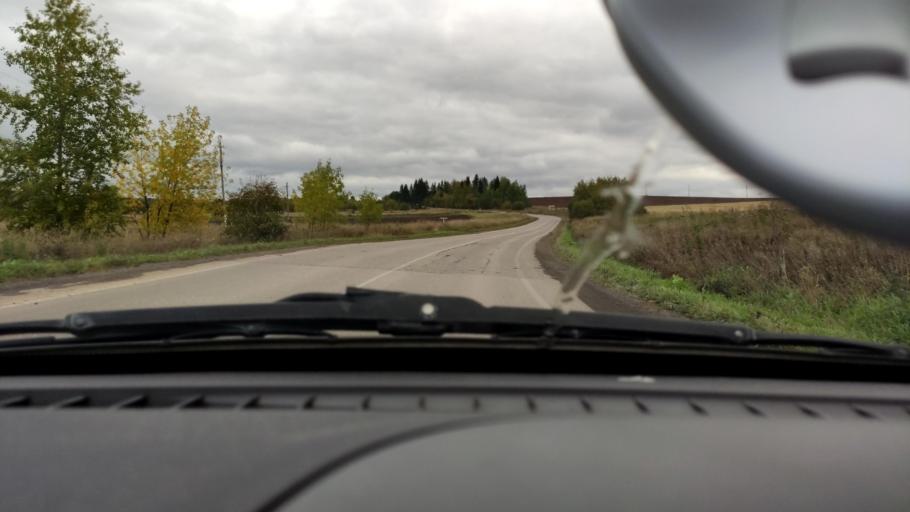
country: RU
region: Perm
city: Lobanovo
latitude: 57.8547
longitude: 56.3210
